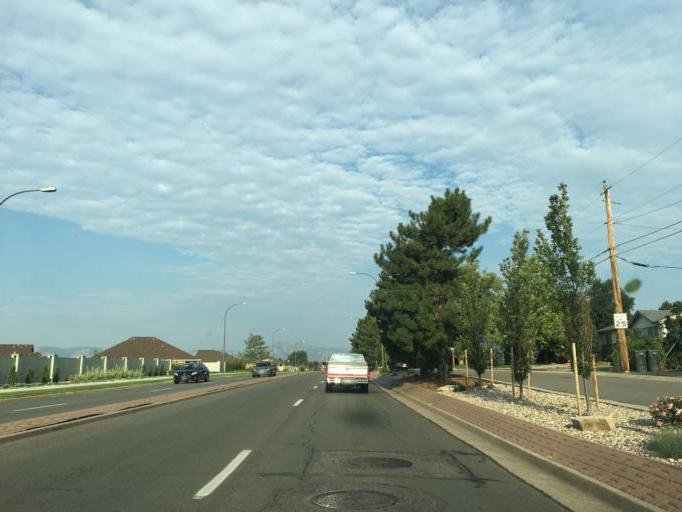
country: US
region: Colorado
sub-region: Jefferson County
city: Lakewood
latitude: 39.6822
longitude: -105.0740
